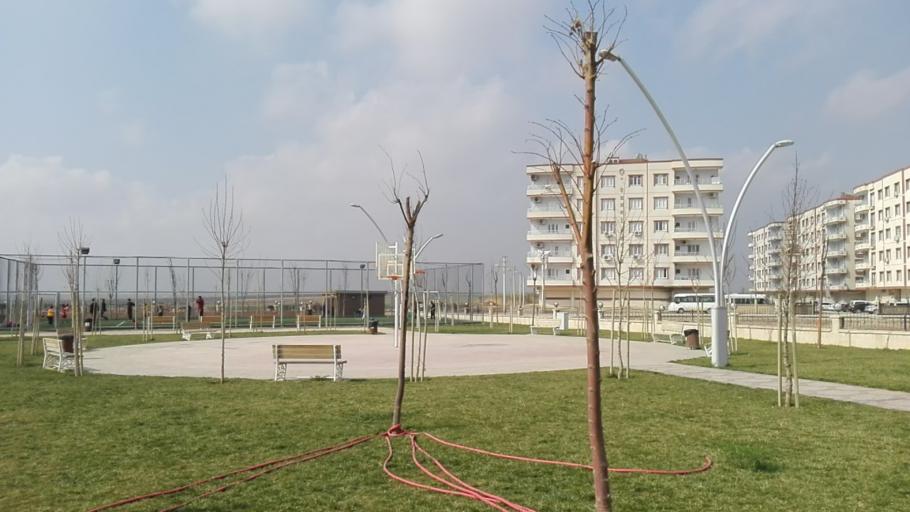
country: TR
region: Mardin
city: Nusaybin
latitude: 37.0822
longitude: 41.2029
